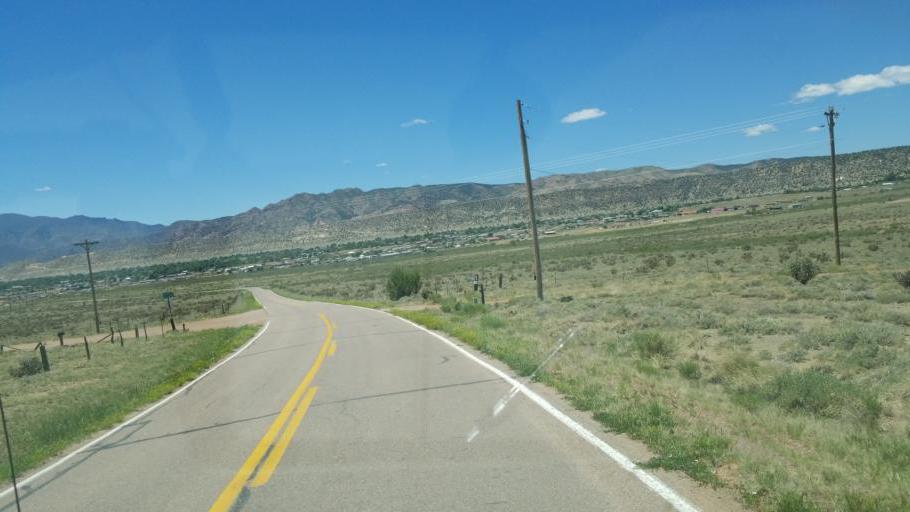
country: US
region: Colorado
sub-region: Fremont County
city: Canon City
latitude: 38.4836
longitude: -105.2176
